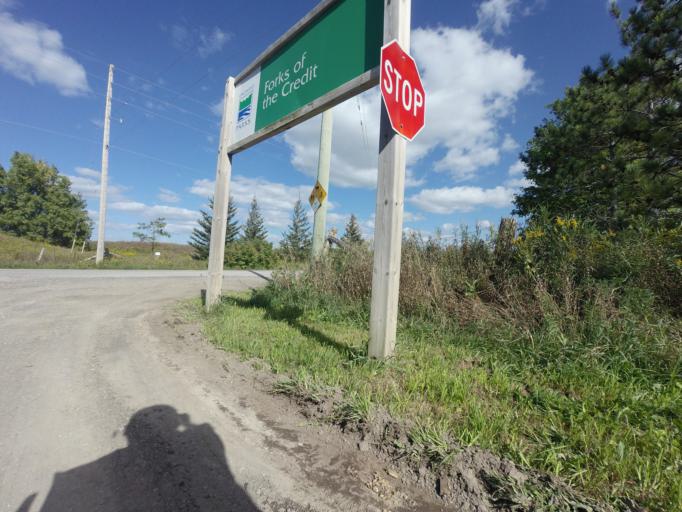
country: CA
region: Ontario
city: Orangeville
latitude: 43.8286
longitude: -80.0016
